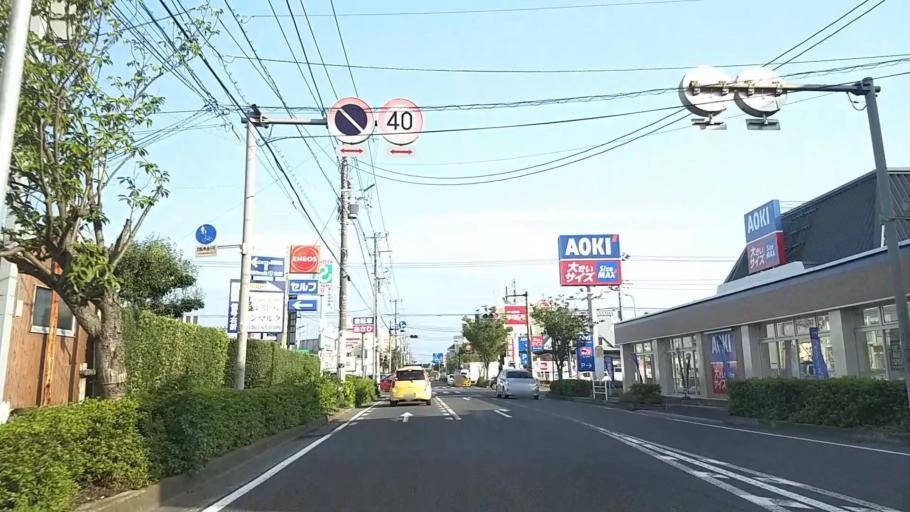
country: JP
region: Kanagawa
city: Hiratsuka
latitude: 35.3289
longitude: 139.3285
